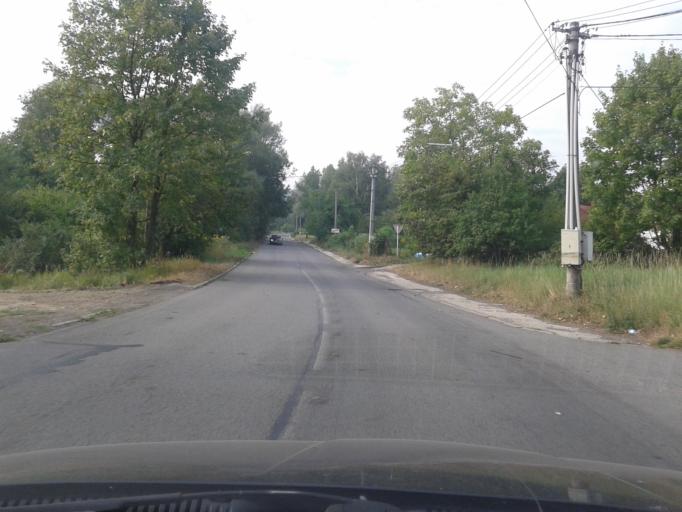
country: CZ
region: Moravskoslezsky
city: Orlova
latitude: 49.8460
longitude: 18.4511
